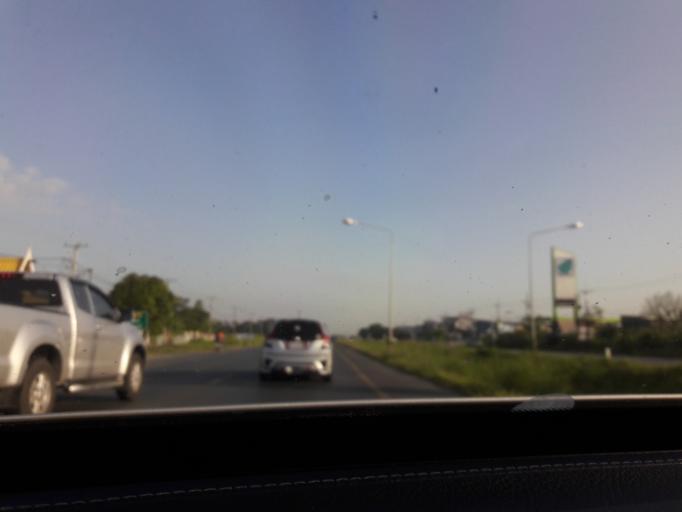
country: TH
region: Phra Nakhon Si Ayutthaya
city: Bang Ban
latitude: 14.4043
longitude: 100.5304
